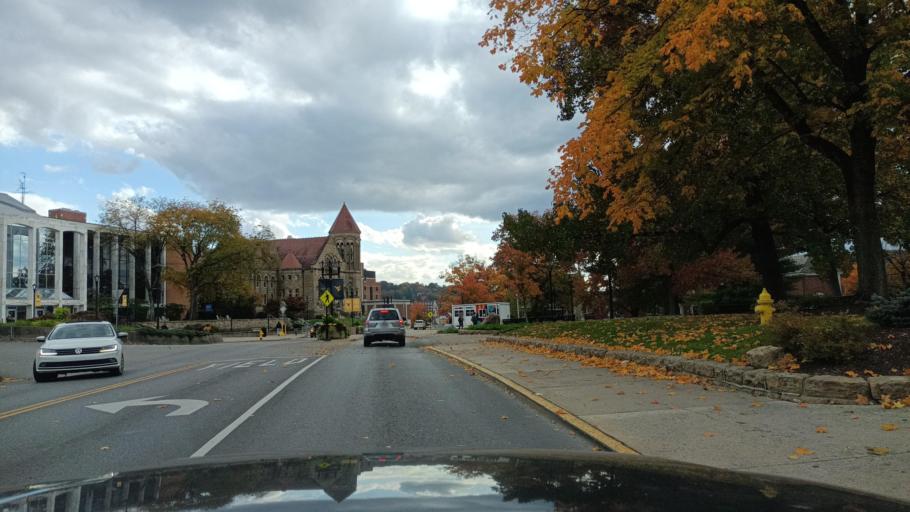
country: US
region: West Virginia
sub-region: Monongalia County
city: Morgantown
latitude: 39.6358
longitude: -79.9543
